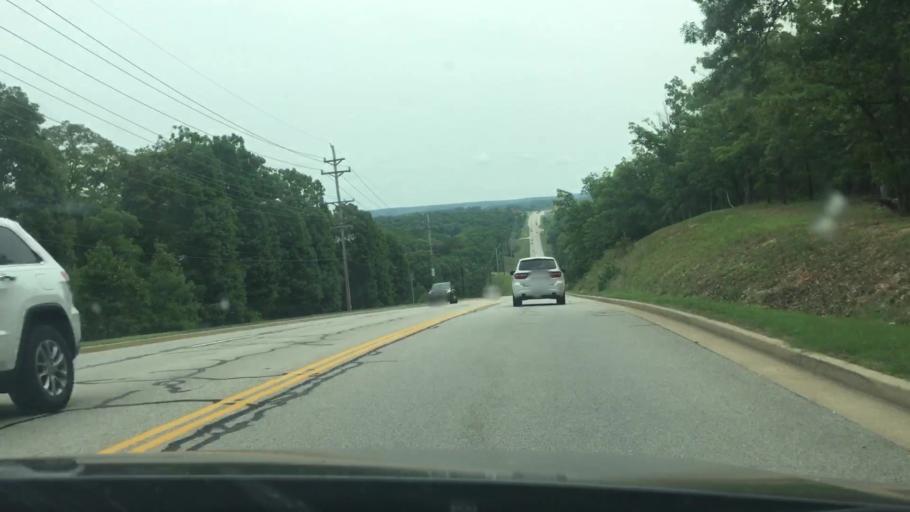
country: US
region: Missouri
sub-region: Miller County
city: Lake Ozark
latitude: 38.1923
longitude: -92.6637
